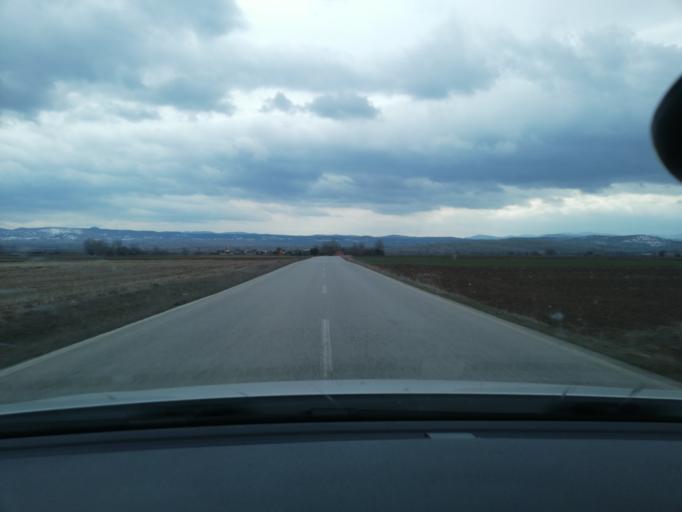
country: TR
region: Bolu
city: Gerede
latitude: 40.7417
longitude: 32.2094
